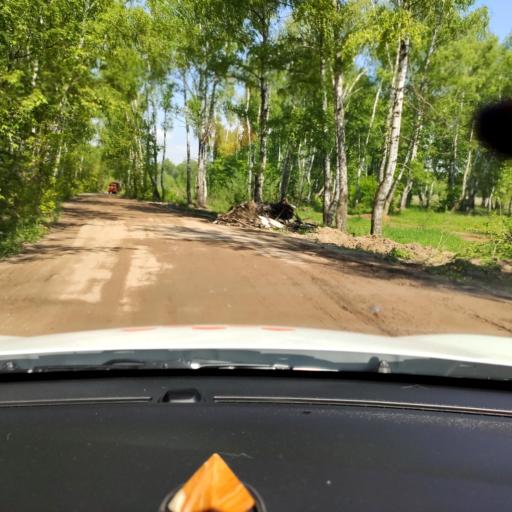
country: RU
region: Tatarstan
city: Stolbishchi
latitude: 55.7077
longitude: 49.1871
